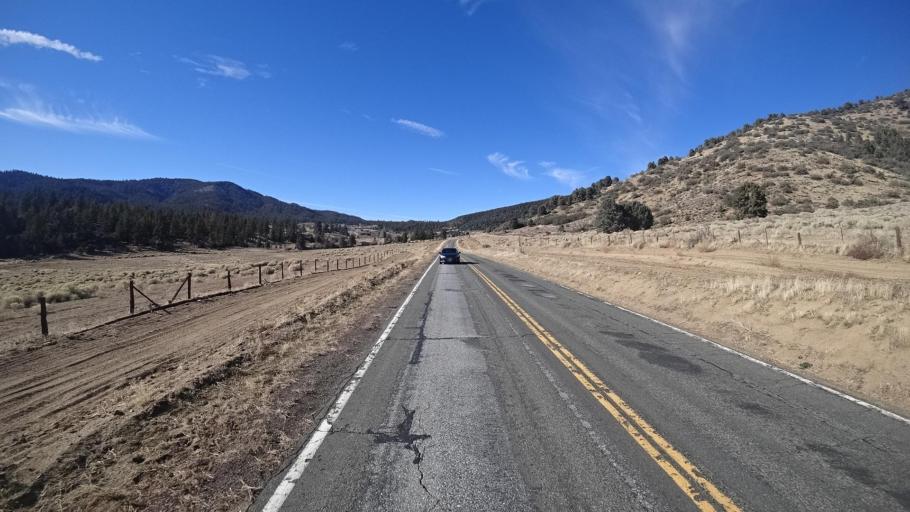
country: US
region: California
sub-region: Kern County
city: Pine Mountain Club
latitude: 34.8398
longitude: -119.0560
